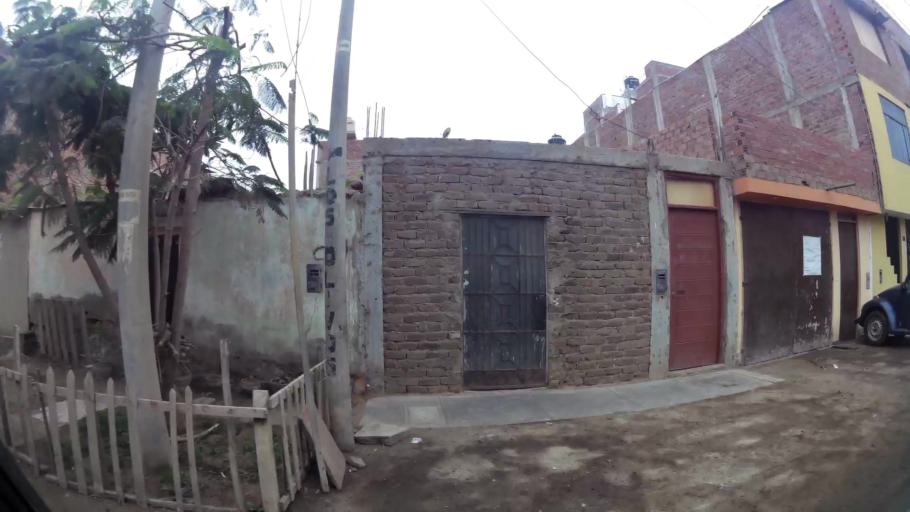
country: PE
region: La Libertad
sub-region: Provincia de Trujillo
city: Buenos Aires
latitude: -8.1241
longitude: -79.0457
